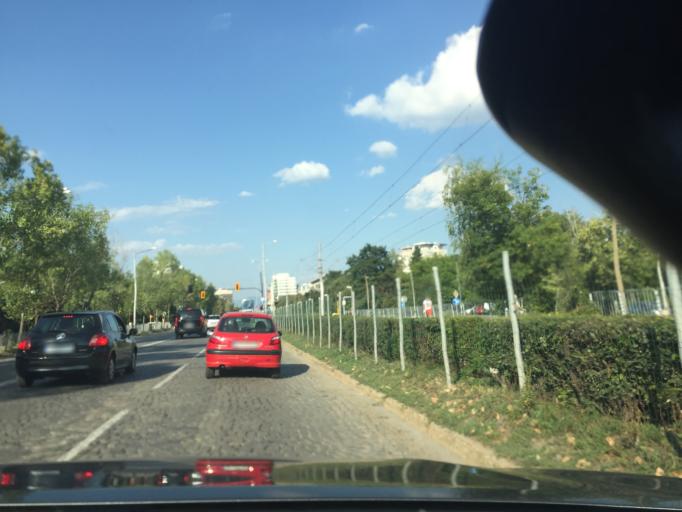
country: BG
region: Sofia-Capital
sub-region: Stolichna Obshtina
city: Sofia
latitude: 42.6825
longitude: 23.2918
